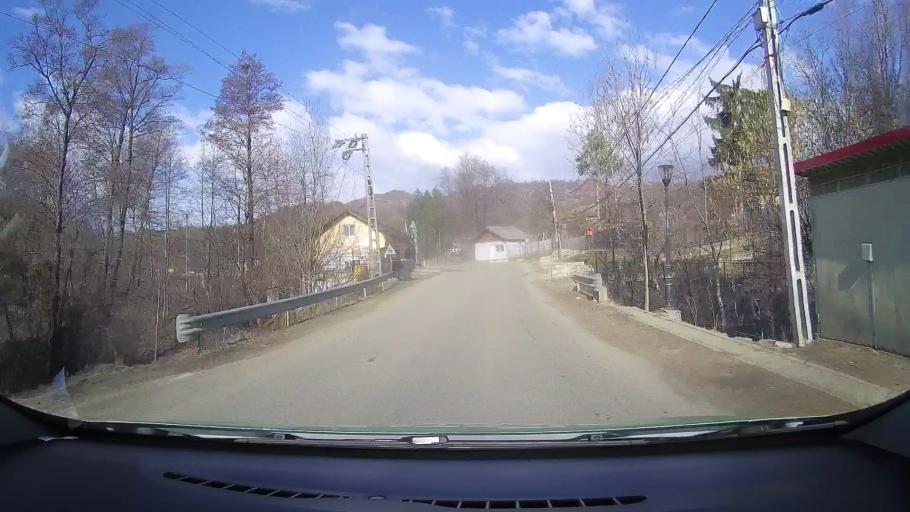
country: RO
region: Dambovita
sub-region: Comuna Varfuri
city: Varfuri
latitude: 45.0896
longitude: 25.4938
